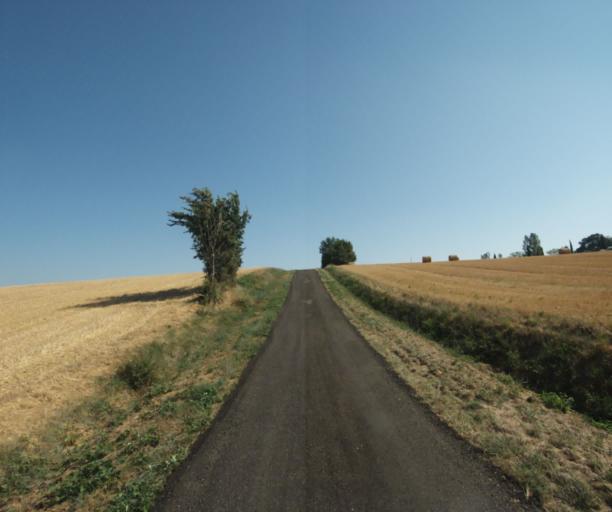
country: FR
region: Midi-Pyrenees
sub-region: Departement de la Haute-Garonne
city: Saint-Felix-Lauragais
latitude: 43.5020
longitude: 1.9175
